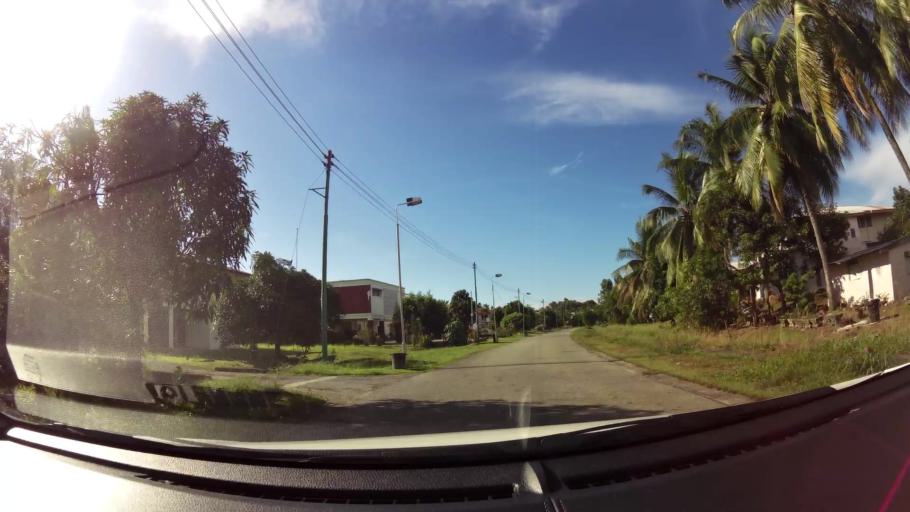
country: BN
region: Brunei and Muara
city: Bandar Seri Begawan
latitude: 4.9645
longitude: 114.9530
